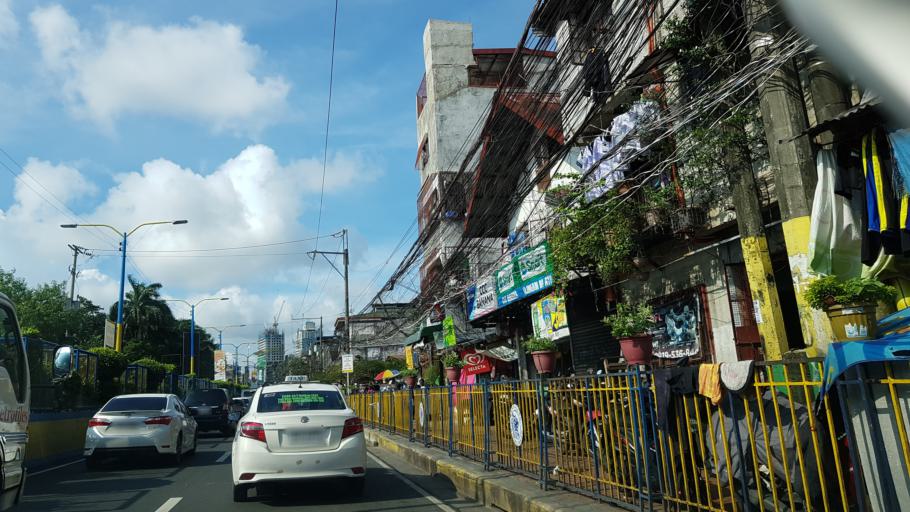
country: PH
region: Metro Manila
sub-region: Mandaluyong
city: Mandaluyong City
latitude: 14.5819
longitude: 121.0369
